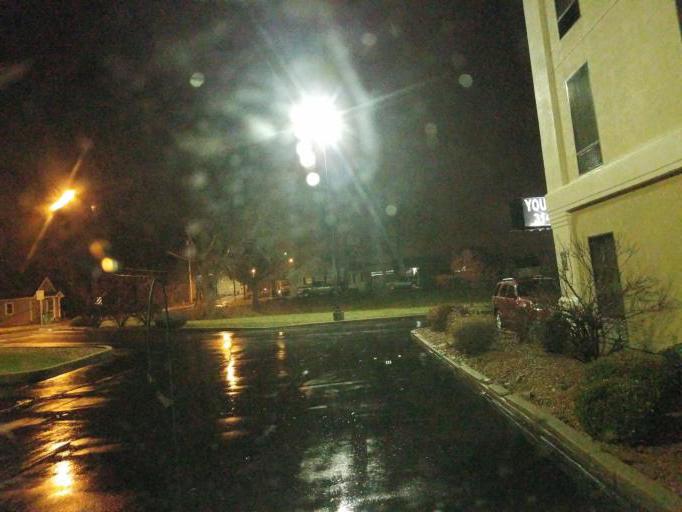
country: US
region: Missouri
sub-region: Franklin County
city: Pacific
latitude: 38.4858
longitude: -90.7560
